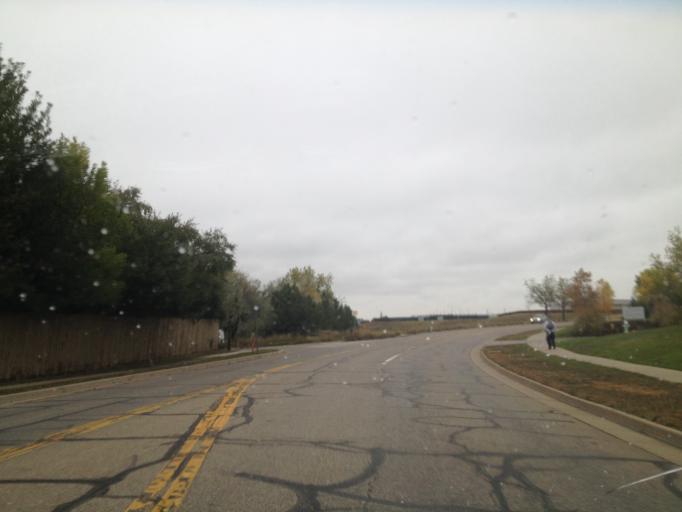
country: US
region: Colorado
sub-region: Boulder County
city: Boulder
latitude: 40.0329
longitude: -105.2346
